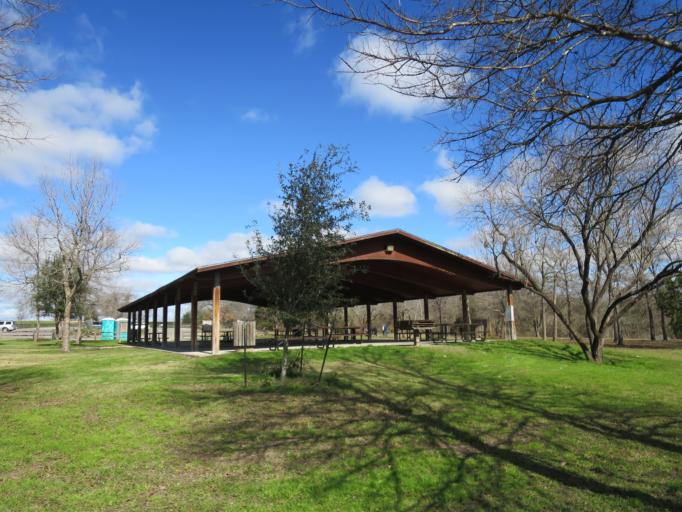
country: US
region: Texas
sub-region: Williamson County
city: Round Rock
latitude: 30.5335
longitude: -97.6259
